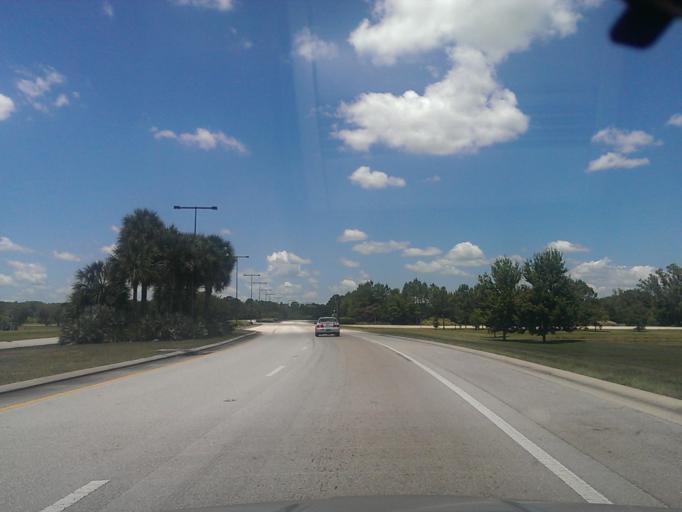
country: US
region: Florida
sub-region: Polk County
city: Citrus Ridge
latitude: 28.3728
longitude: -81.5908
